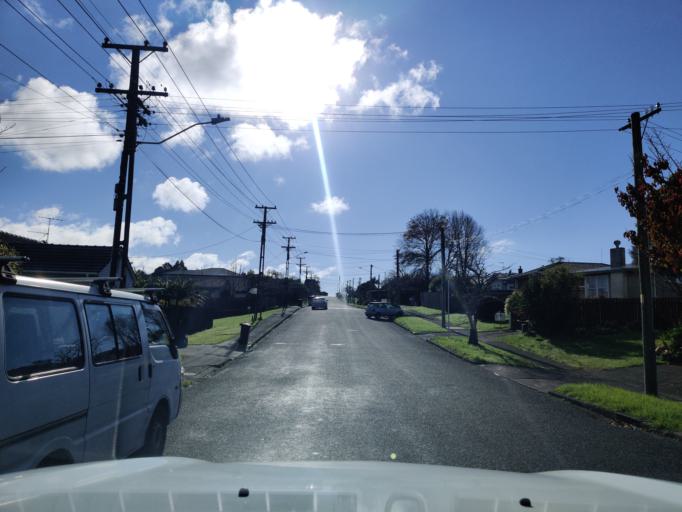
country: NZ
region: Auckland
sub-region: Auckland
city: Tamaki
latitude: -36.9020
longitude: 174.8374
